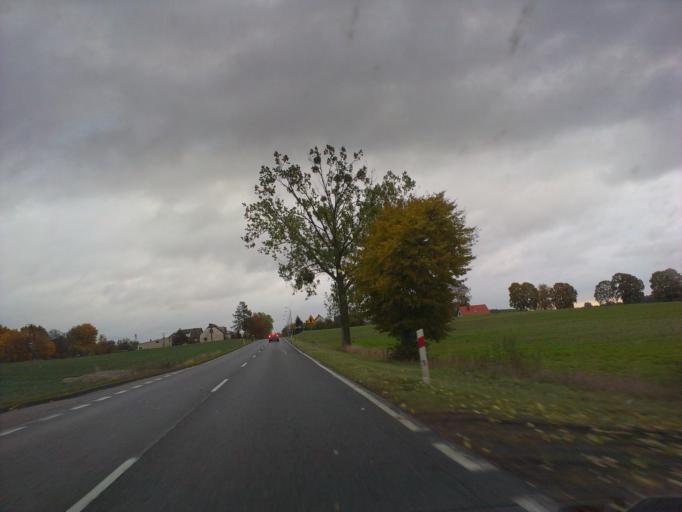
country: PL
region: Kujawsko-Pomorskie
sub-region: Powiat swiecki
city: Bukowiec
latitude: 53.4496
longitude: 18.2407
